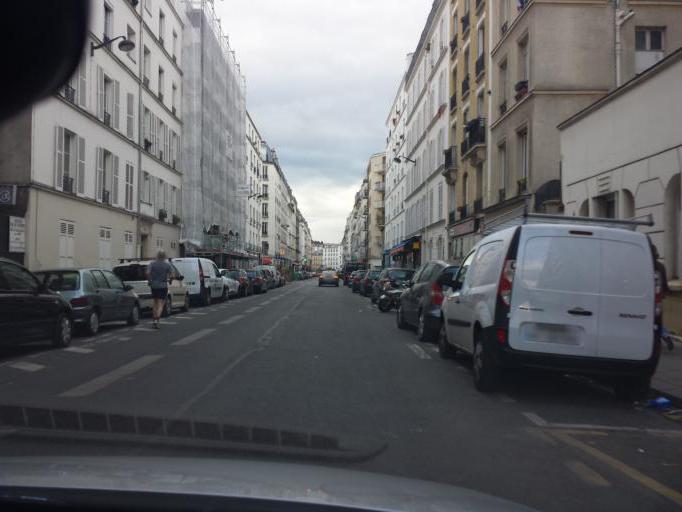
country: FR
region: Ile-de-France
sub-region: Departement du Val-de-Marne
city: Saint-Mande
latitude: 48.8359
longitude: 2.3957
